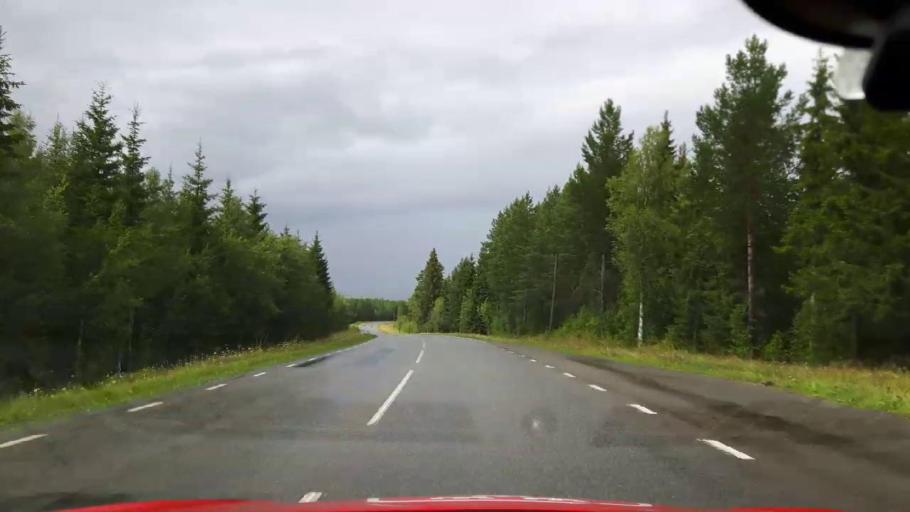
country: SE
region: Jaemtland
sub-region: Krokoms Kommun
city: Krokom
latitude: 63.3332
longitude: 14.2846
